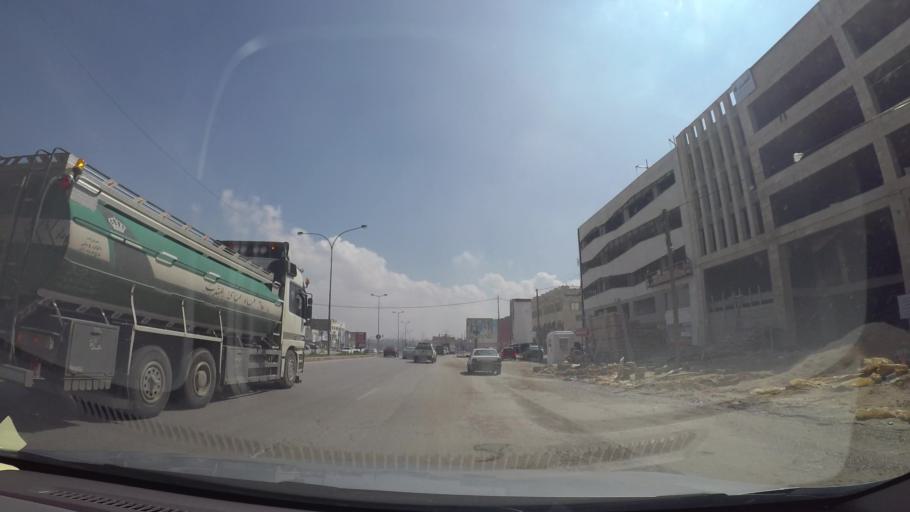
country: JO
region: Amman
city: Al Bunayyat ash Shamaliyah
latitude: 31.9006
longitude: 35.8943
